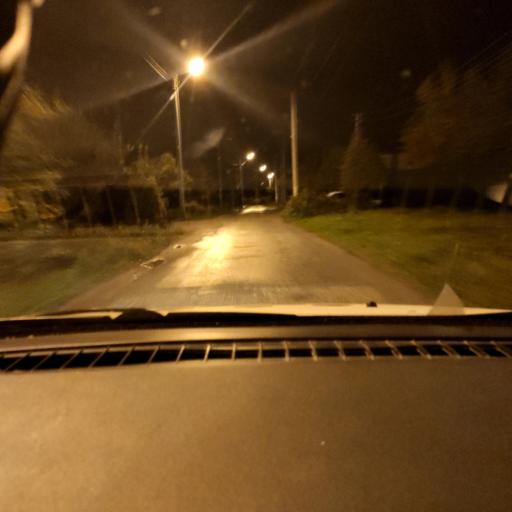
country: RU
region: Perm
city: Kondratovo
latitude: 58.0297
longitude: 56.0023
